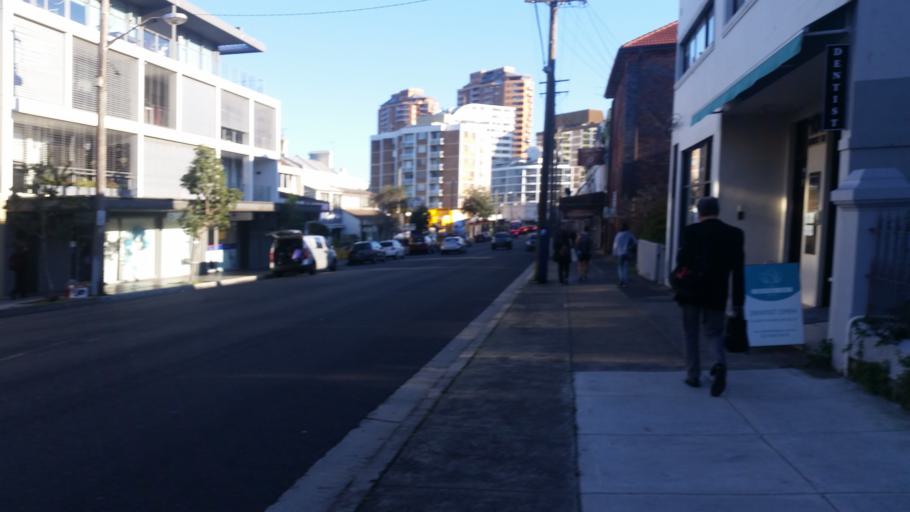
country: AU
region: New South Wales
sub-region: Waverley
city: Bondi Junction
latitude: -33.8956
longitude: 151.2508
